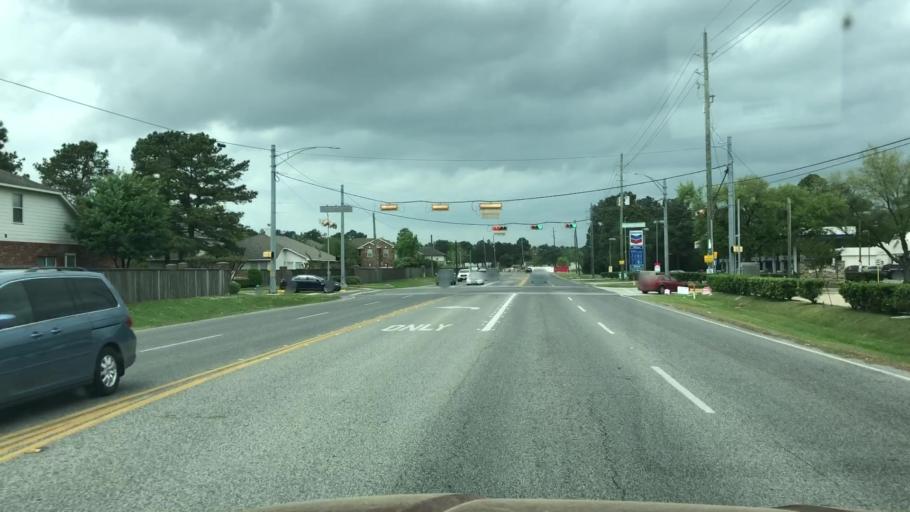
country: US
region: Texas
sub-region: Harris County
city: Spring
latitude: 30.0569
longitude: -95.4954
